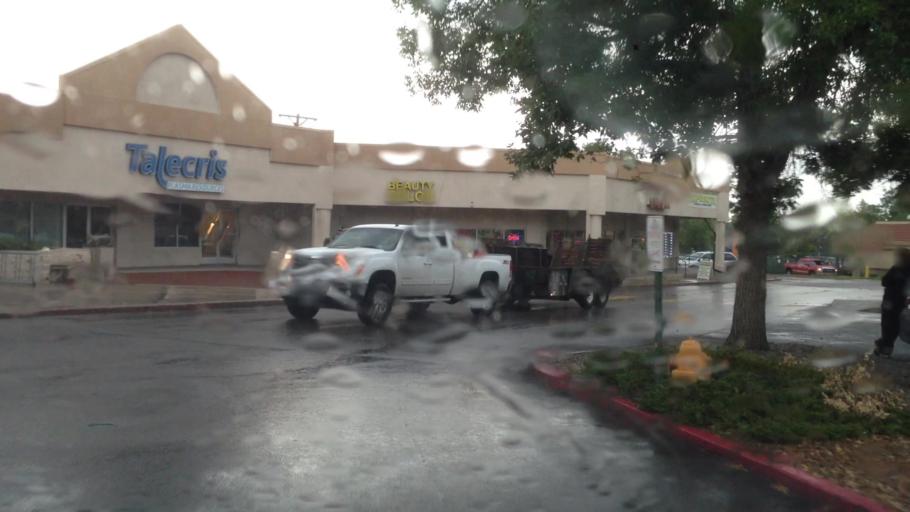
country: US
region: Colorado
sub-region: Jefferson County
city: Lakewood
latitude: 39.7128
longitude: -105.0544
